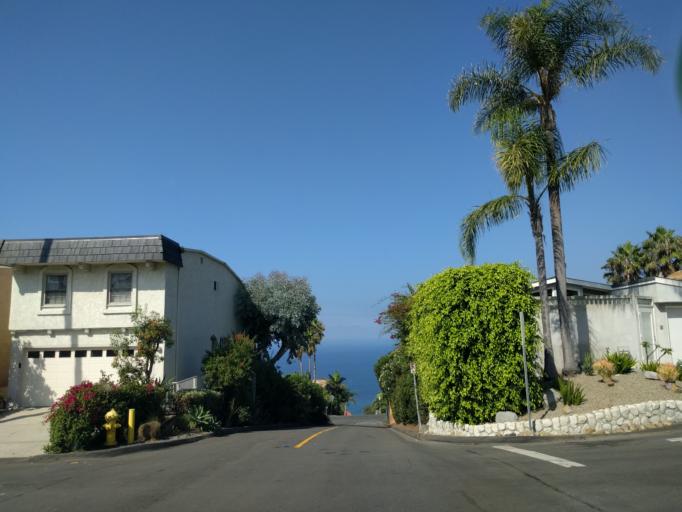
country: US
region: California
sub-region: Orange County
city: Laguna Beach
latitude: 33.5307
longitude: -117.7602
